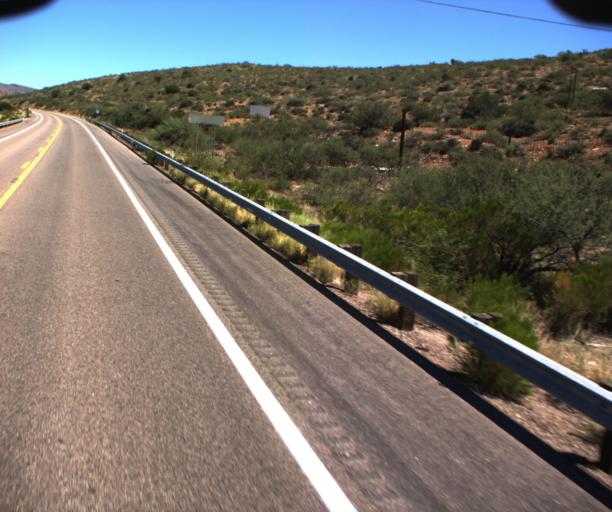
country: US
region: Arizona
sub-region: Gila County
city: Globe
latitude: 33.4483
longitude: -110.7212
